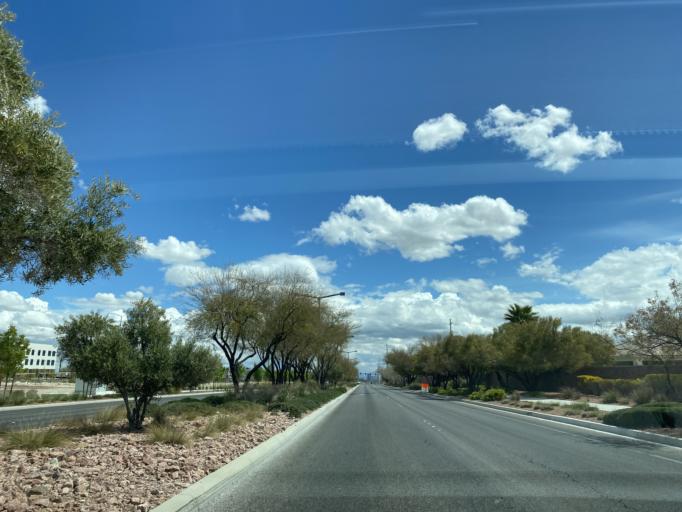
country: US
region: Nevada
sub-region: Clark County
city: Summerlin South
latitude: 36.1153
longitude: -115.3190
